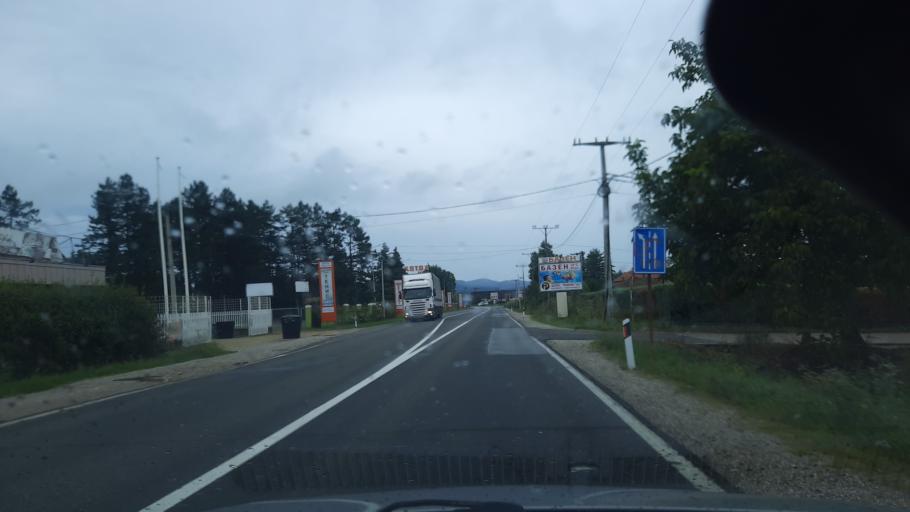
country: RS
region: Central Serbia
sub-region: Sumadijski Okrug
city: Knic
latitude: 43.9354
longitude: 20.7787
